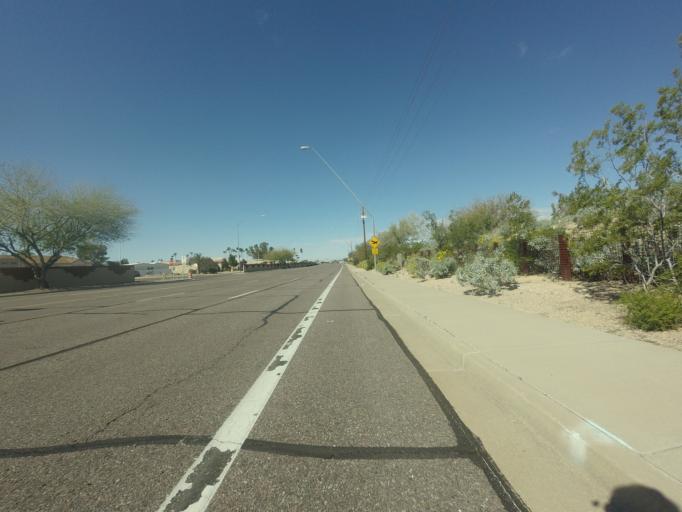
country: US
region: Arizona
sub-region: Maricopa County
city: Mesa
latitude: 33.4665
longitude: -111.7140
